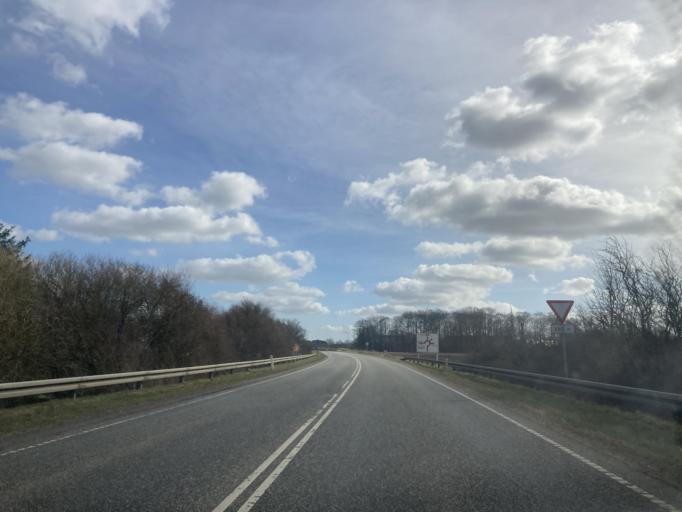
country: DK
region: Central Jutland
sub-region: Hedensted Kommune
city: Torring
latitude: 55.8504
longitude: 9.4730
